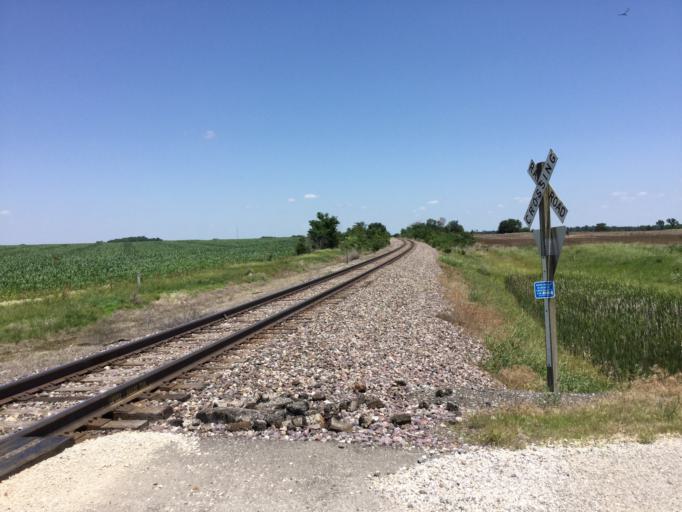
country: US
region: Kansas
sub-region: Anderson County
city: Garnett
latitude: 38.1828
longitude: -95.0485
